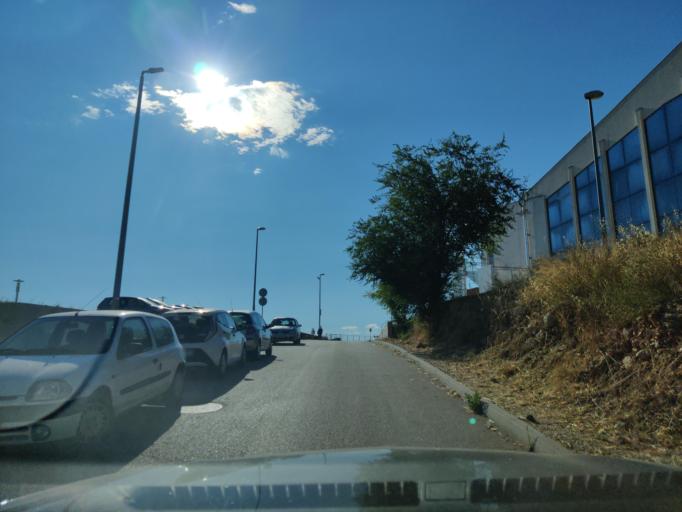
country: HR
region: Sibensko-Kniniska
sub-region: Grad Sibenik
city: Sibenik
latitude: 43.7415
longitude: 15.8853
